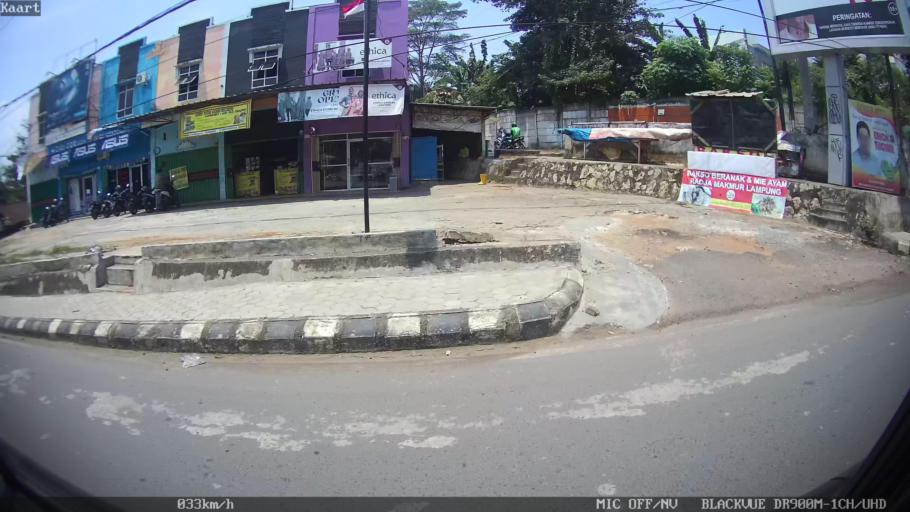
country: ID
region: Lampung
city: Kedaton
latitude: -5.3702
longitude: 105.2380
